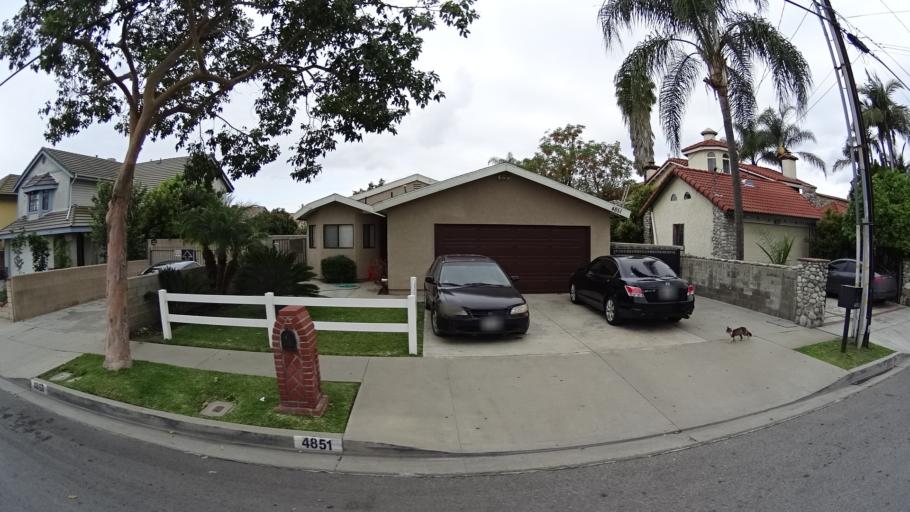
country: US
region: California
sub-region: Los Angeles County
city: Irwindale
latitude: 34.1012
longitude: -117.9485
